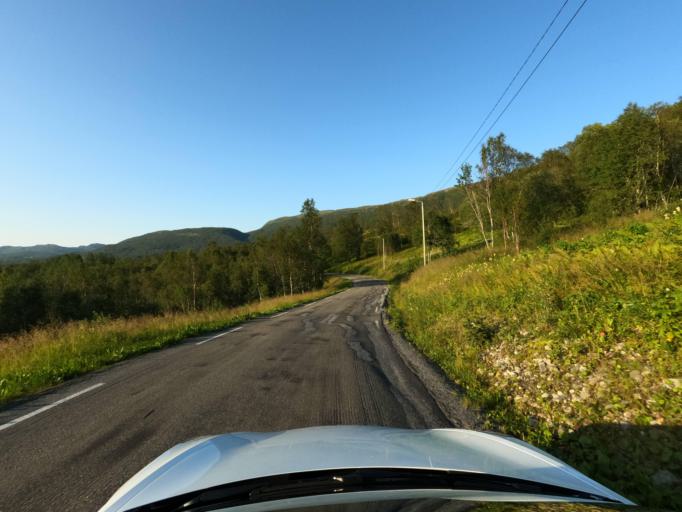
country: NO
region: Nordland
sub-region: Ballangen
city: Ballangen
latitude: 68.5214
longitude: 16.7610
